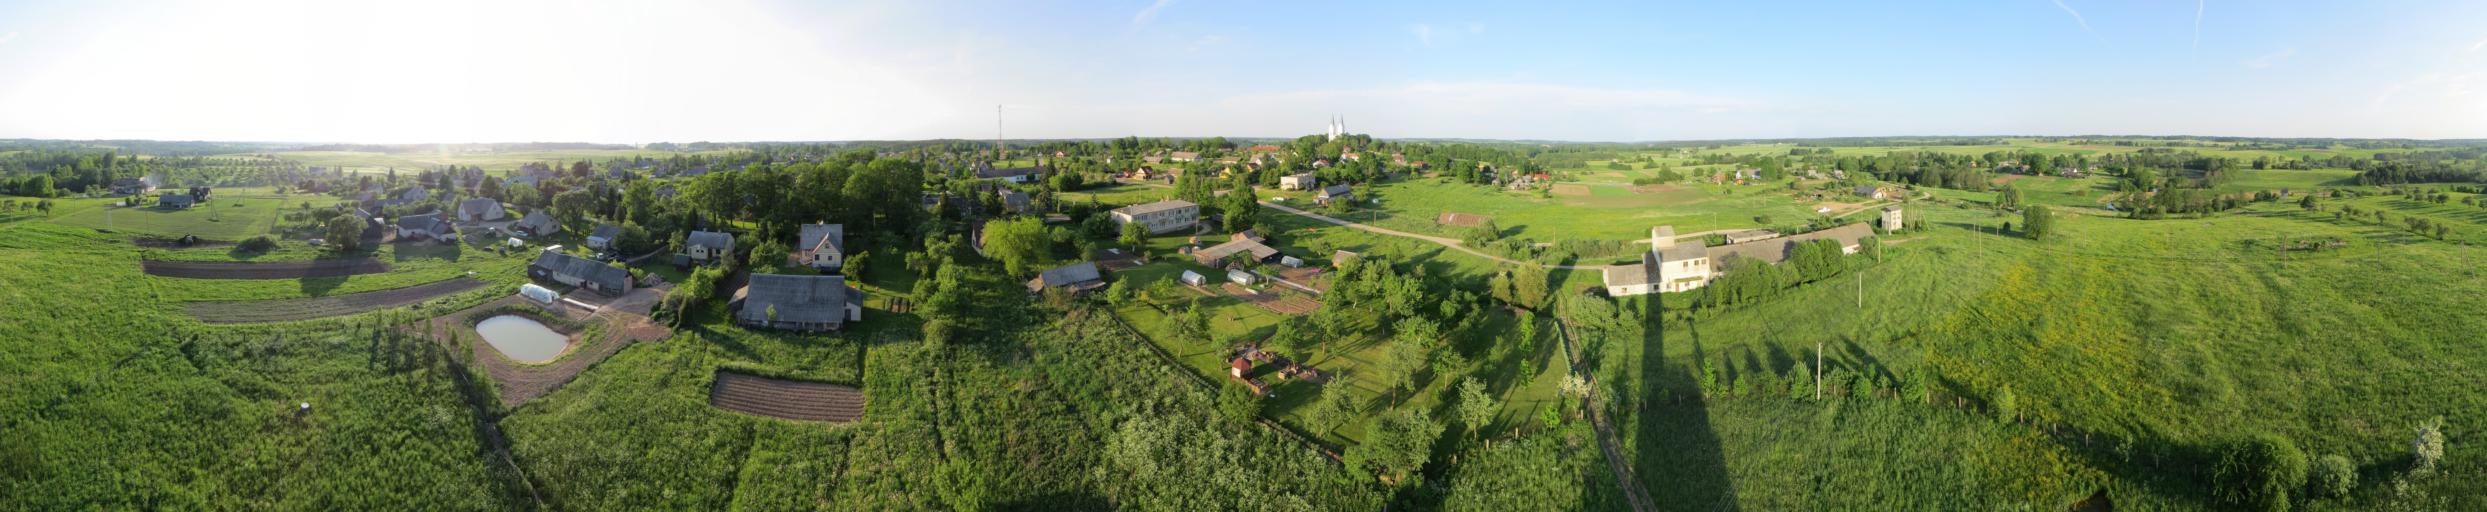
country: LT
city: Moletai
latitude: 55.3484
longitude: 25.2873
